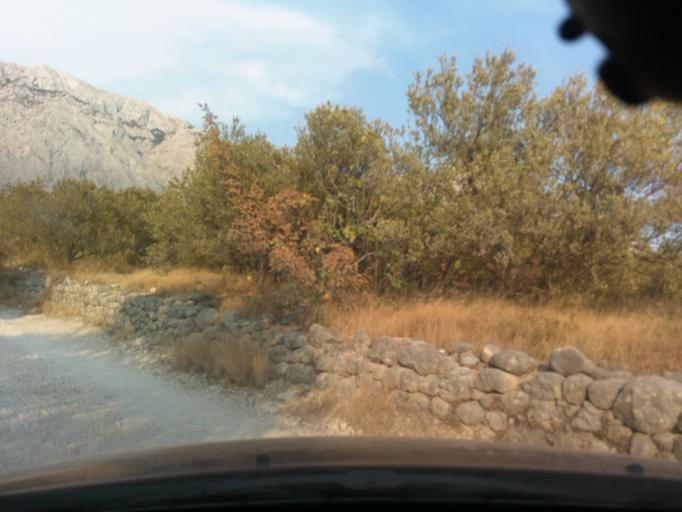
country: HR
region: Splitsko-Dalmatinska
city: Baska Voda
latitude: 43.3492
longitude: 16.9543
